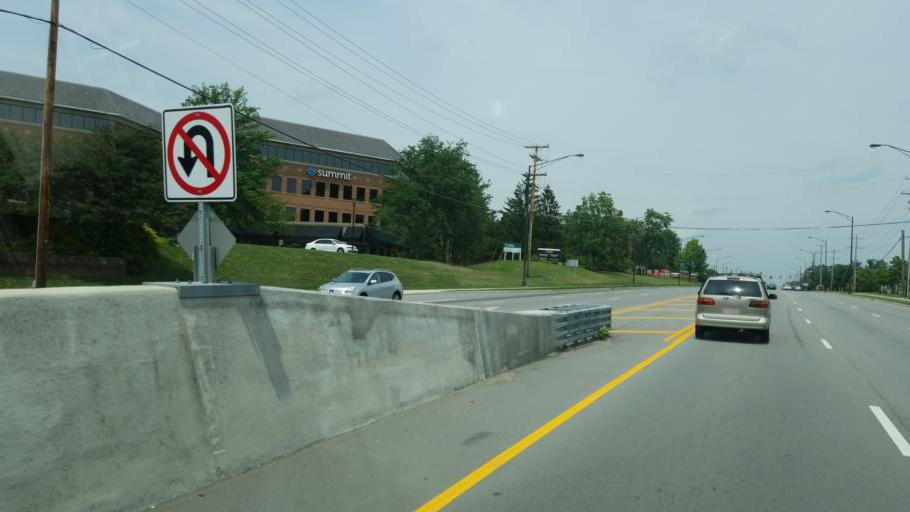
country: US
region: Ohio
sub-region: Franklin County
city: Worthington
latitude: 40.1270
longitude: -83.0163
